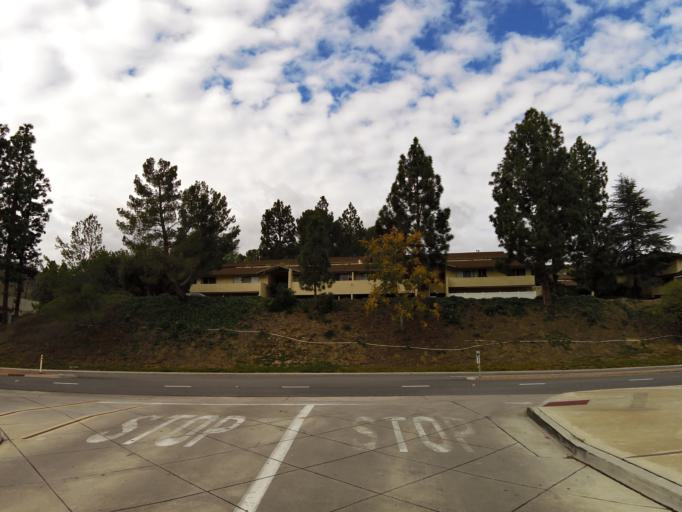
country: US
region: California
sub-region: Ventura County
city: Thousand Oaks
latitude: 34.1859
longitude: -118.8764
